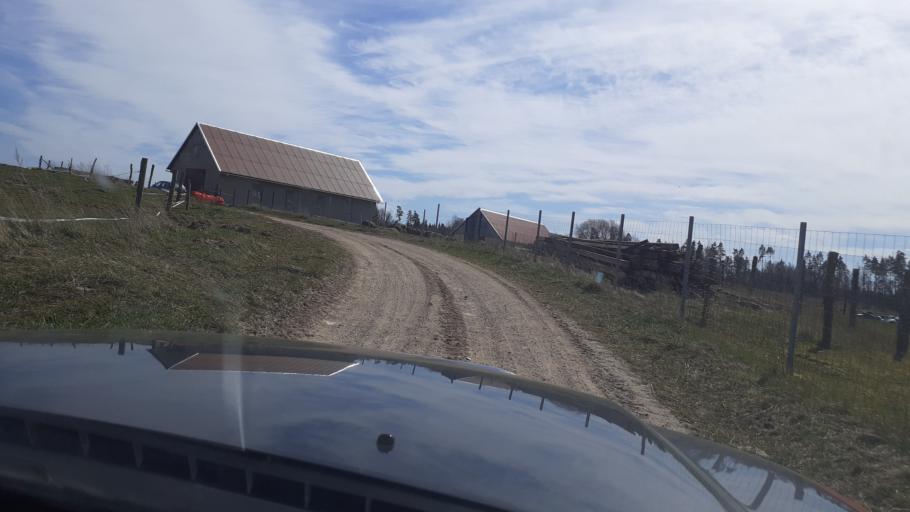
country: LV
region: Skrunda
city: Skrunda
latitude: 56.8322
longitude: 22.0073
